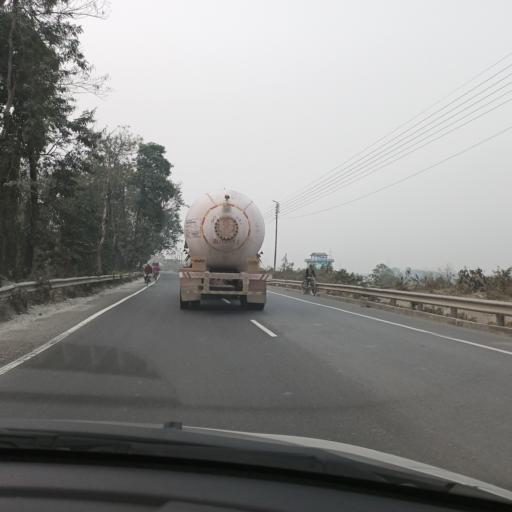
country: IN
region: West Bengal
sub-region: Darjiling
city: Shiliguri
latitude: 26.6515
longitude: 88.4064
